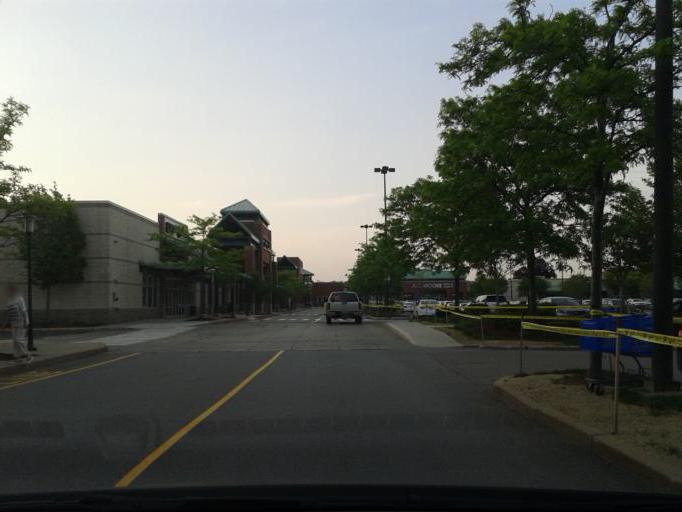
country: US
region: Massachusetts
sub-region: Middlesex County
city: Framingham
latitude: 42.3022
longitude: -71.3960
